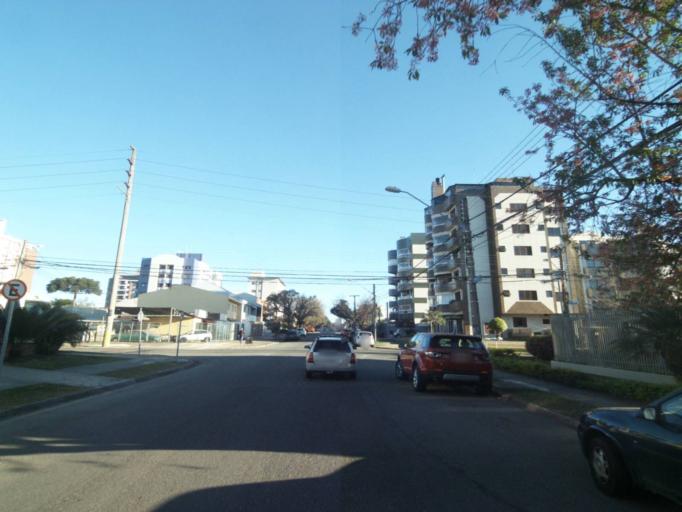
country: BR
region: Parana
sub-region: Curitiba
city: Curitiba
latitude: -25.4583
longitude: -49.2961
